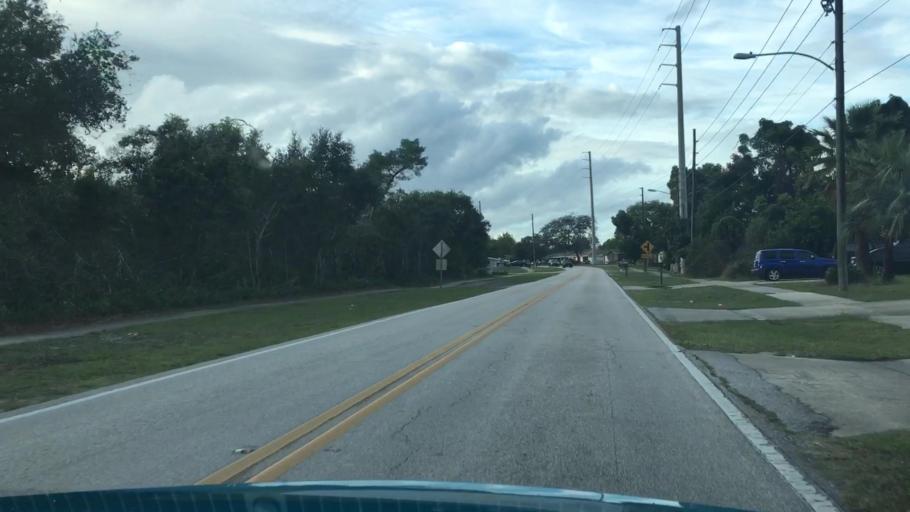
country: US
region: Florida
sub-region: Volusia County
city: Deltona
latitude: 28.8975
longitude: -81.2351
